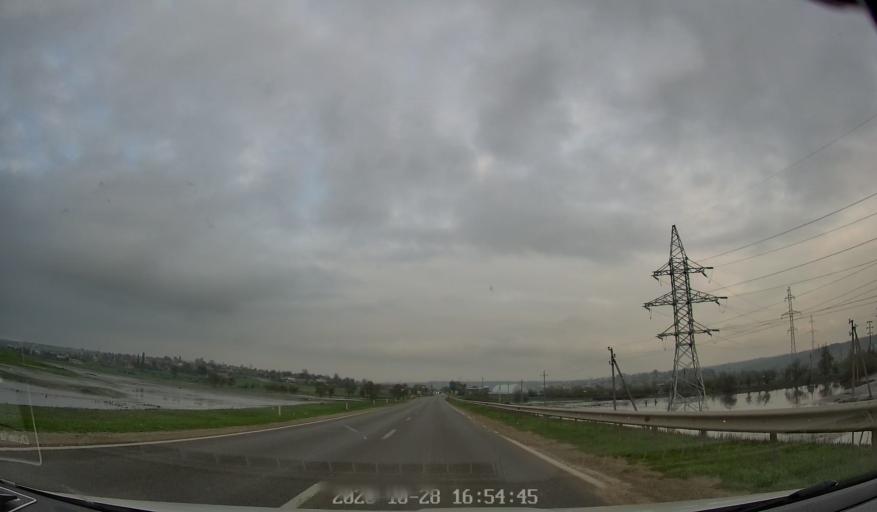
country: MD
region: Gagauzia
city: Bugeac
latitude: 46.3569
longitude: 28.6574
